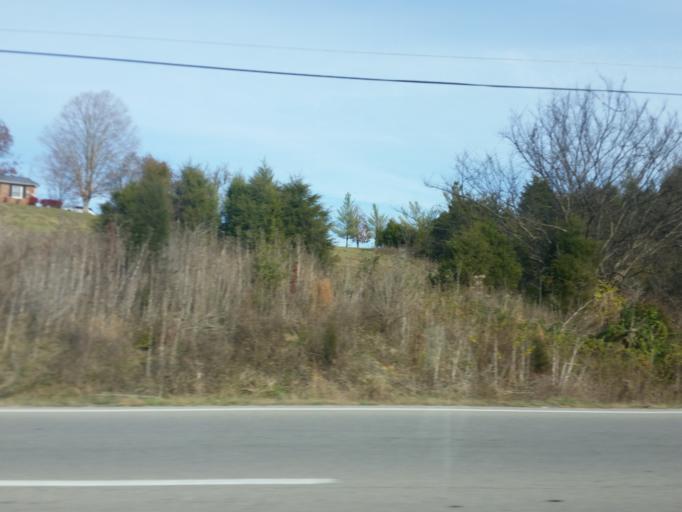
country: US
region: Kentucky
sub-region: Campbell County
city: Claryville
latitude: 38.8193
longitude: -84.3595
